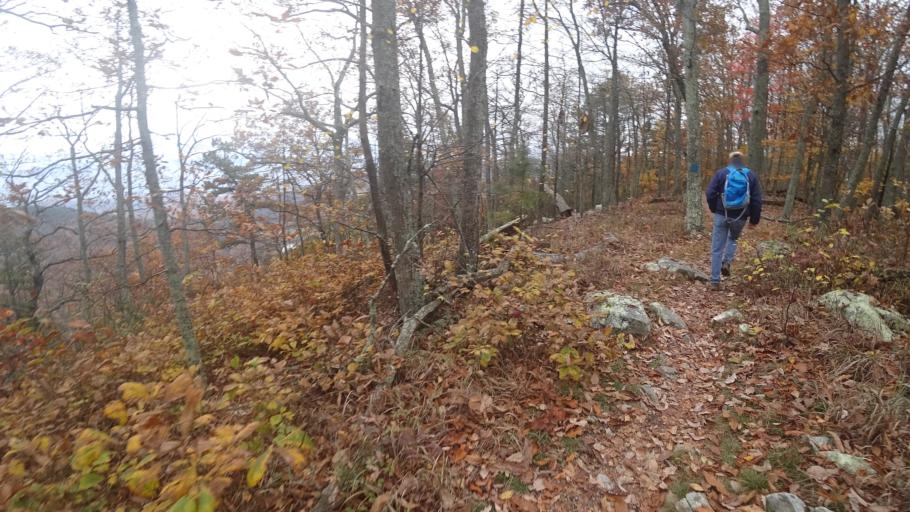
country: US
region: Virginia
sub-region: Rockingham County
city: Massanutten
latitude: 38.4201
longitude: -78.7511
